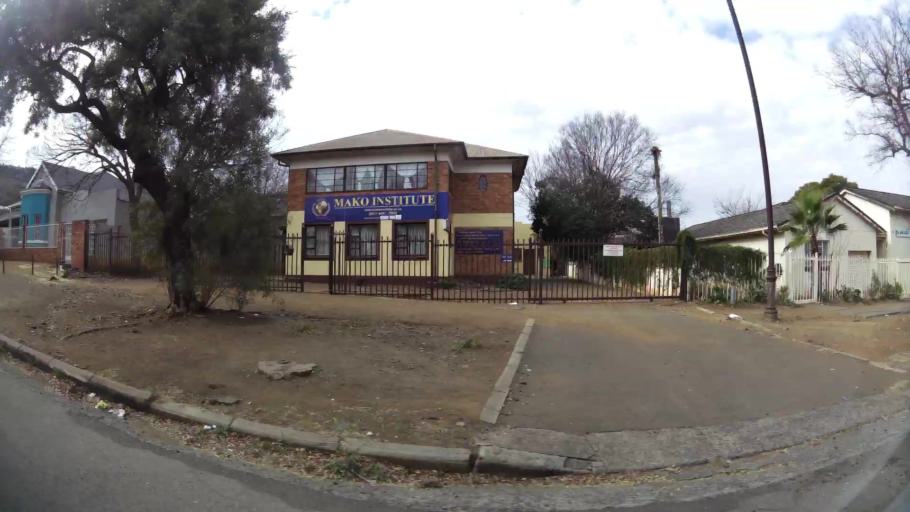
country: ZA
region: Orange Free State
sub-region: Mangaung Metropolitan Municipality
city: Bloemfontein
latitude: -29.1099
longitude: 26.2283
